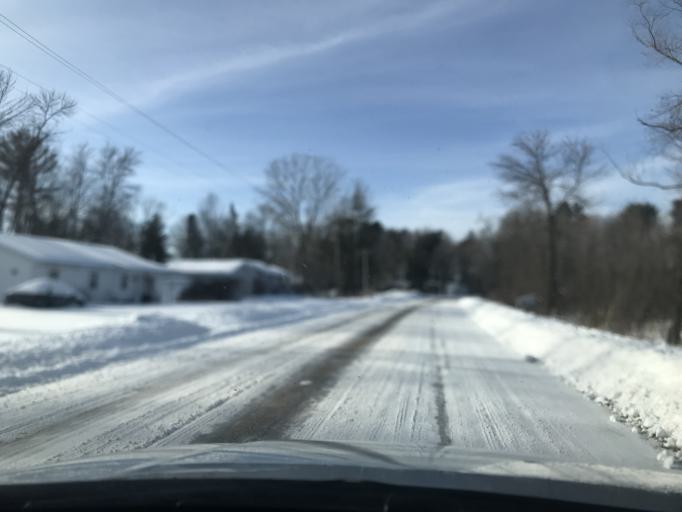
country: US
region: Wisconsin
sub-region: Oconto County
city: Oconto Falls
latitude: 45.1552
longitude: -88.1909
